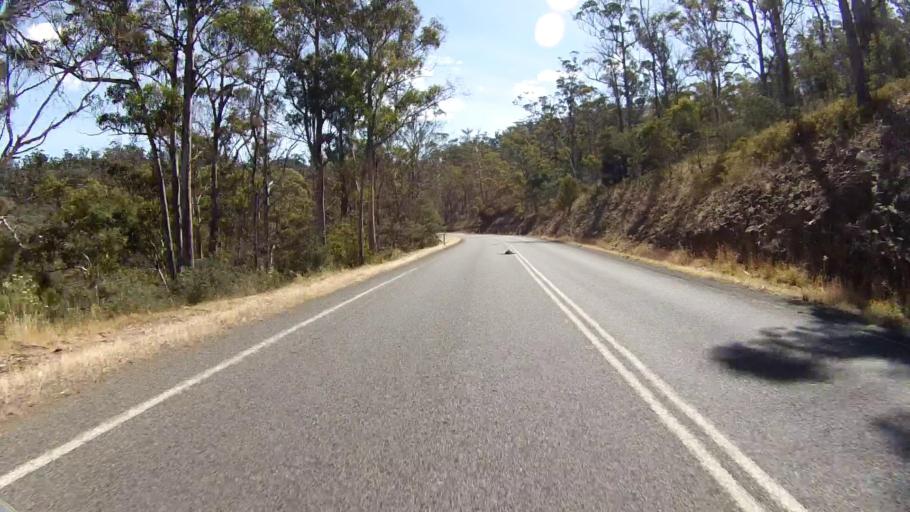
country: AU
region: Tasmania
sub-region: Sorell
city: Sorell
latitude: -42.6108
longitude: 147.6689
